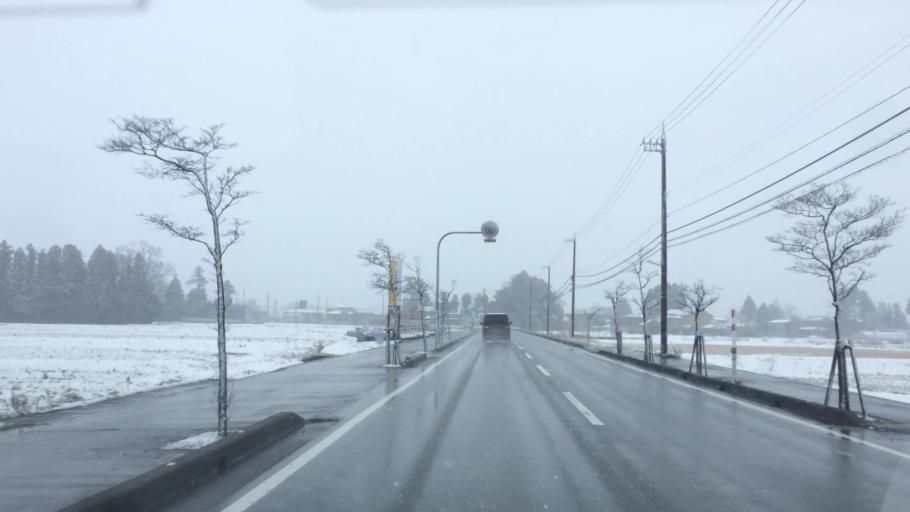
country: JP
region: Toyama
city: Toyama-shi
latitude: 36.6296
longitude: 137.2262
